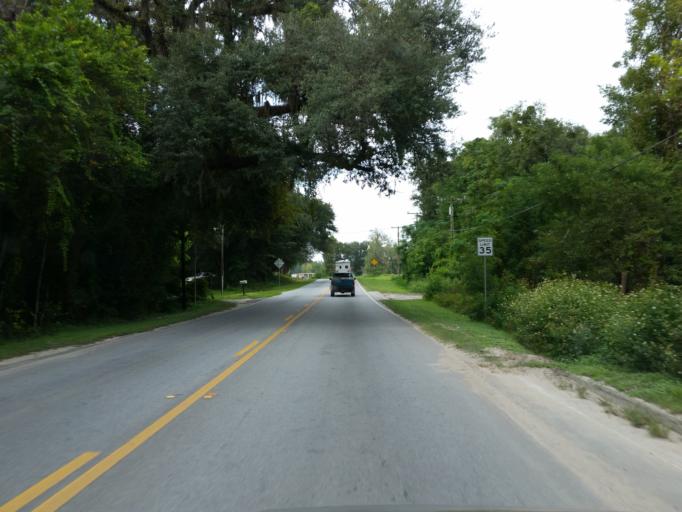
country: US
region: Florida
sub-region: Suwannee County
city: Live Oak
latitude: 30.3080
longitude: -82.9839
